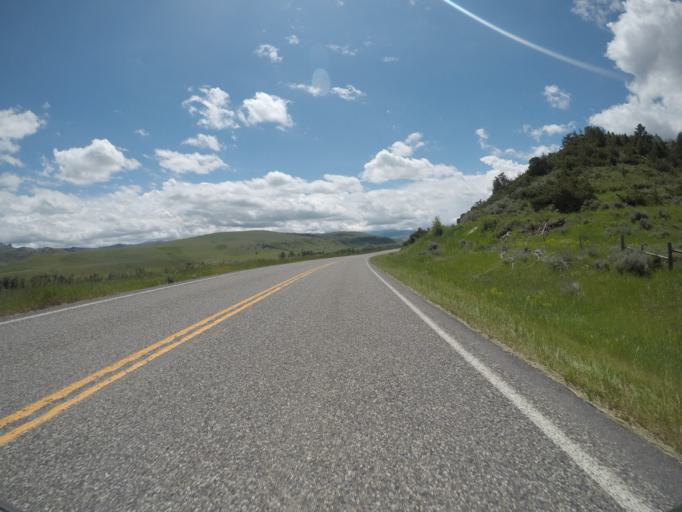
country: US
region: Montana
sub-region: Sweet Grass County
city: Big Timber
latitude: 45.6769
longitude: -110.0886
